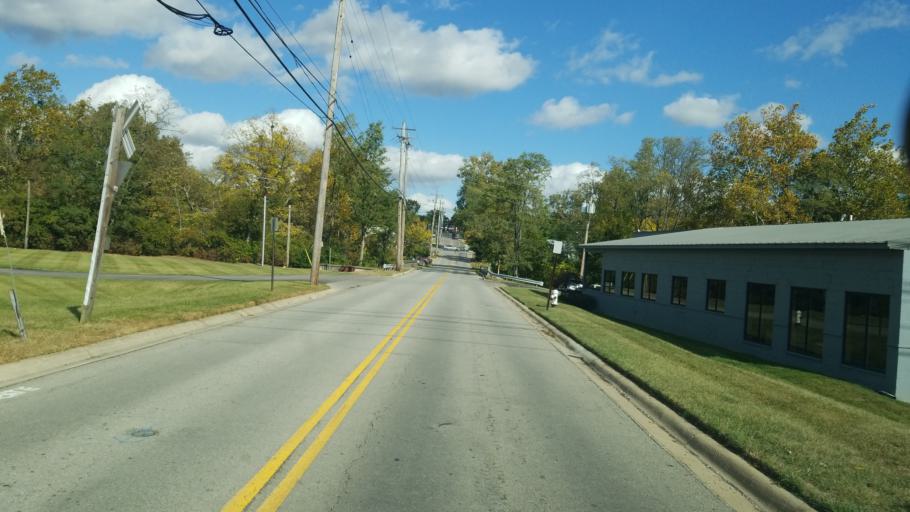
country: US
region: Ohio
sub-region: Warren County
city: Lebanon
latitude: 39.4319
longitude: -84.2157
